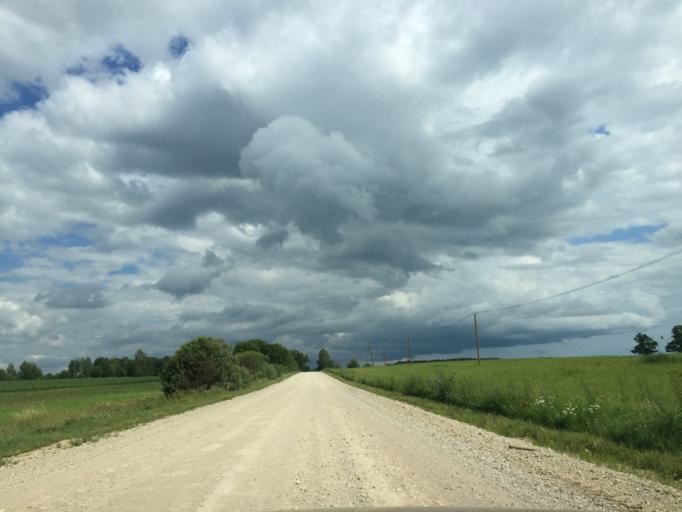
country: LV
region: Malpils
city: Malpils
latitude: 56.8565
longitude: 25.0347
